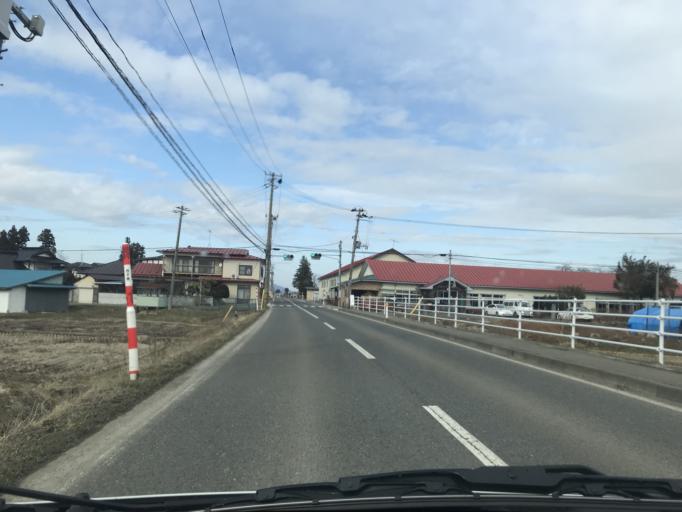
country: JP
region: Iwate
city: Hanamaki
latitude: 39.3487
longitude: 141.0480
